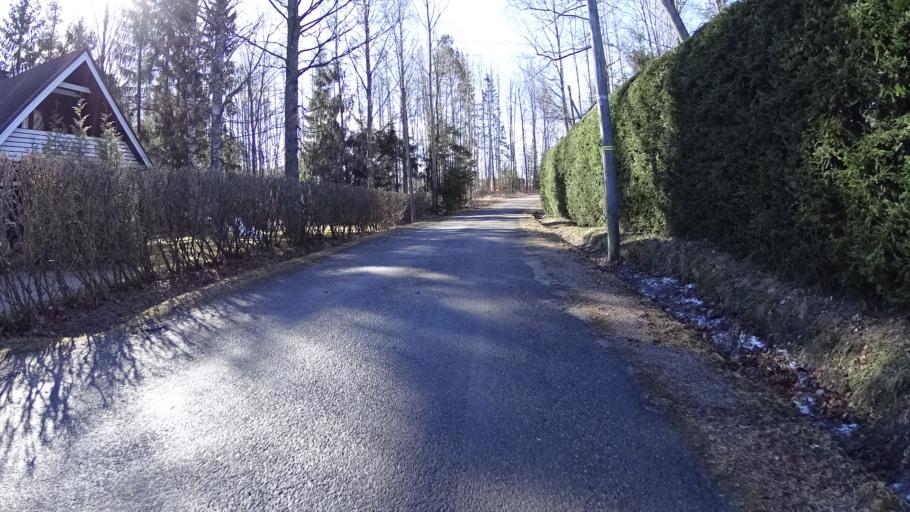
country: FI
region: Uusimaa
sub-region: Helsinki
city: Teekkarikylae
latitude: 60.2643
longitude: 24.8855
